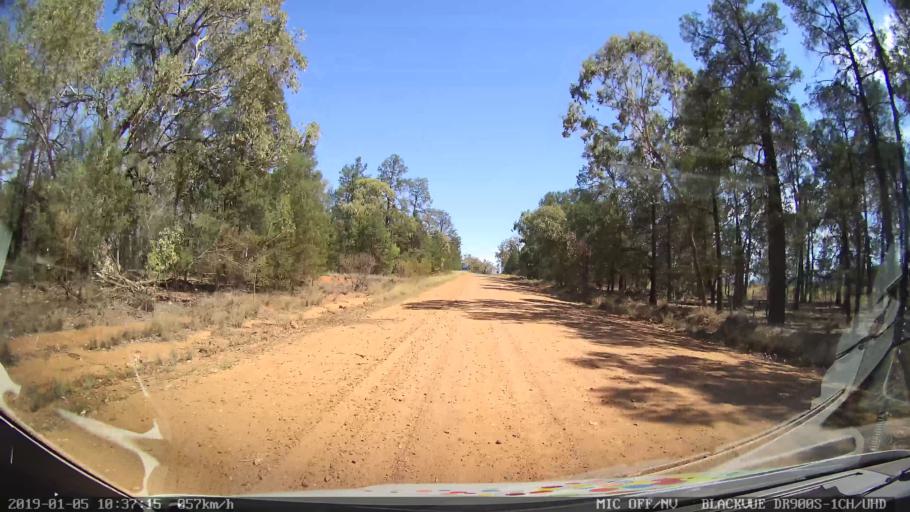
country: AU
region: New South Wales
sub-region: Gilgandra
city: Gilgandra
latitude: -31.4760
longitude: 148.9222
